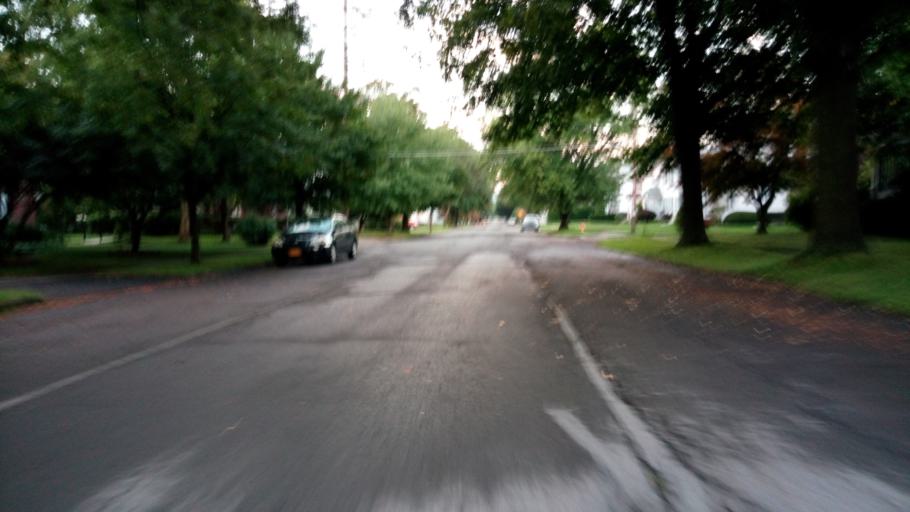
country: US
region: New York
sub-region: Chemung County
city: Elmira
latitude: 42.0949
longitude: -76.8244
